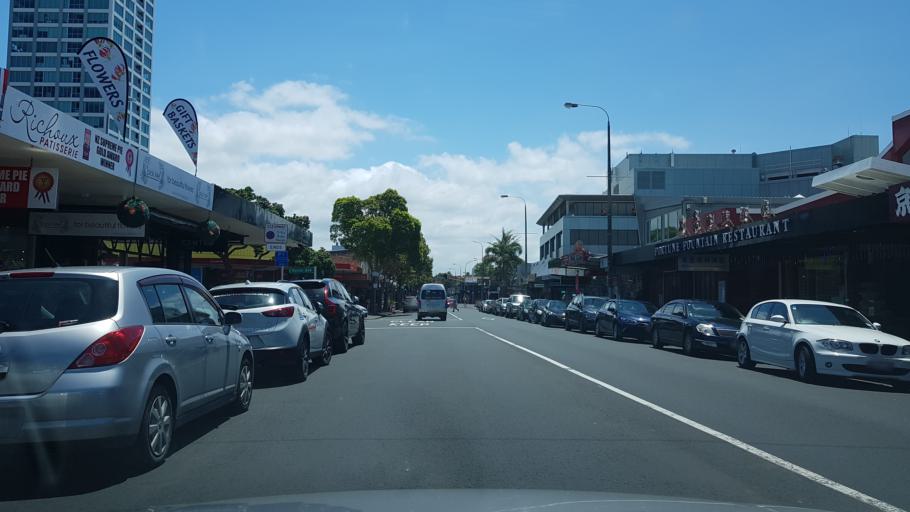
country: NZ
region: Auckland
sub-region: Auckland
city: North Shore
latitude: -36.7904
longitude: 174.7732
